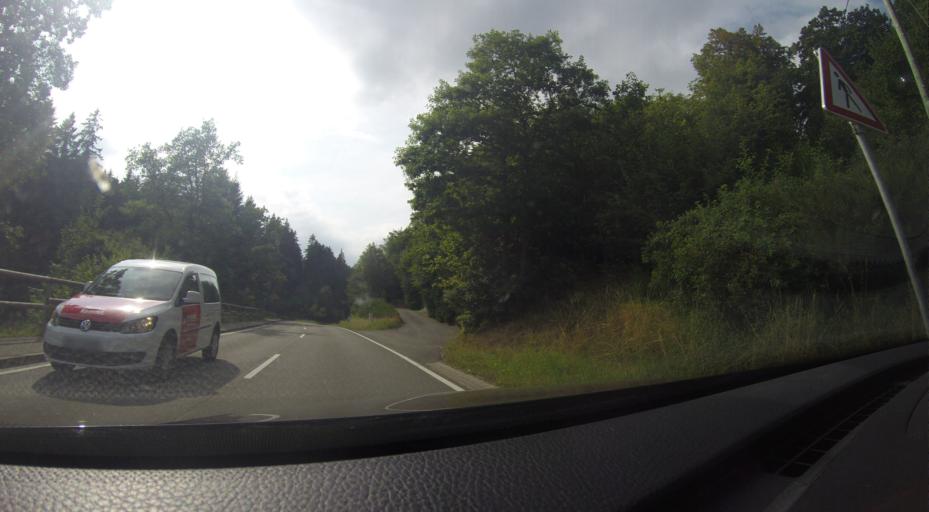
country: DE
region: North Rhine-Westphalia
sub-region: Regierungsbezirk Arnsberg
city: Medebach
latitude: 51.2128
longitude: 8.6386
